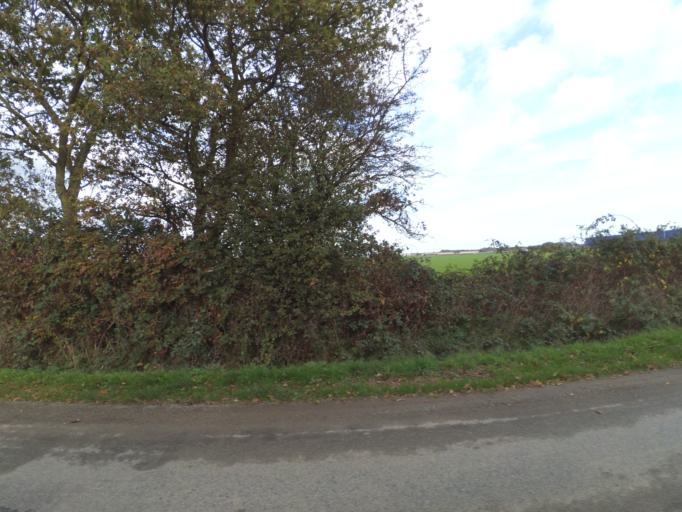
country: FR
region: Pays de la Loire
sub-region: Departement de la Vendee
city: Saint-Hilaire-de-Loulay
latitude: 47.0226
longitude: -1.3578
